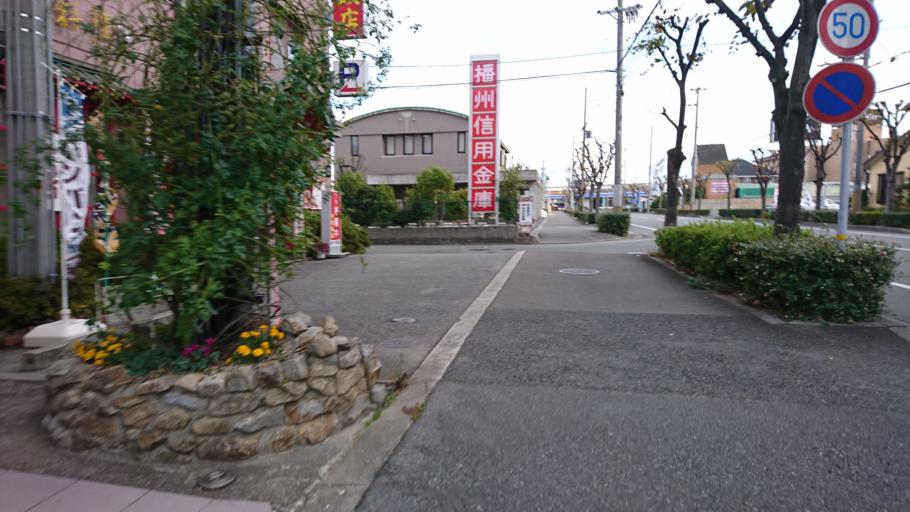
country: JP
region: Hyogo
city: Kakogawacho-honmachi
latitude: 34.7513
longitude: 134.8411
